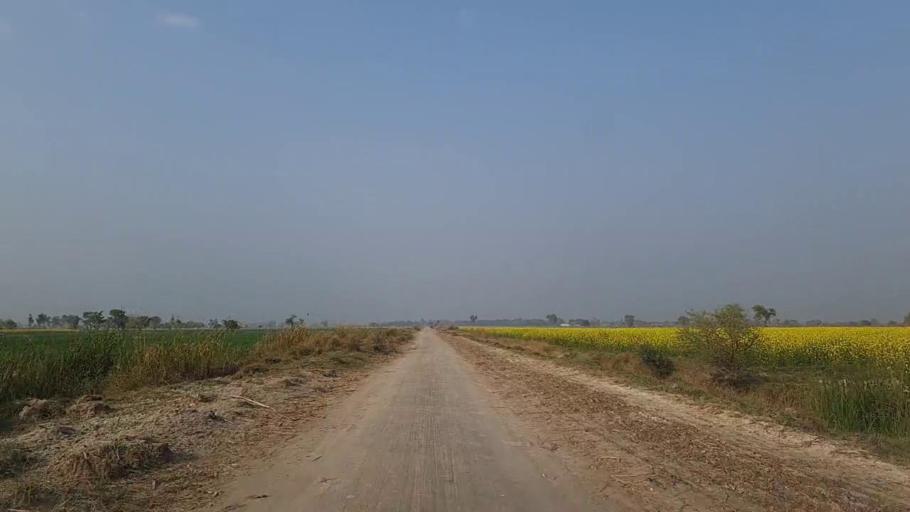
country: PK
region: Sindh
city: Jam Sahib
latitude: 26.3375
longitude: 68.5148
